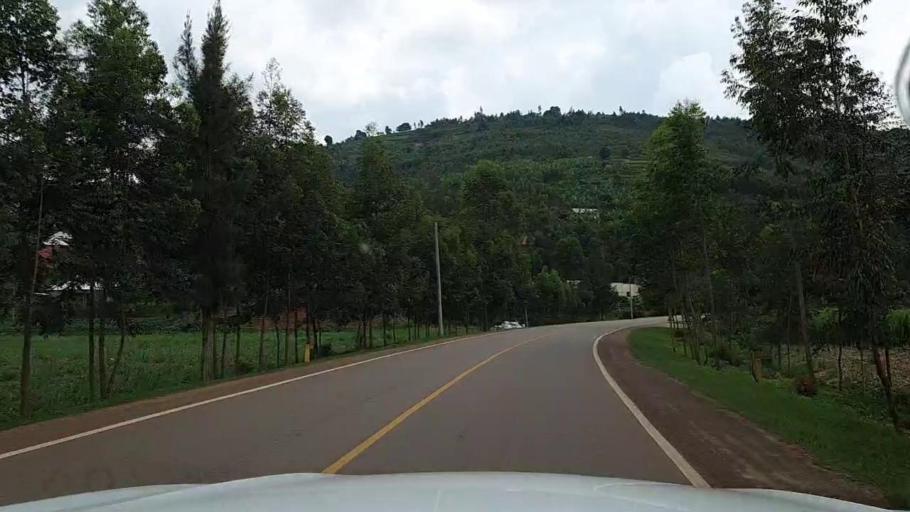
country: RW
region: Kigali
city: Kigali
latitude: -1.8121
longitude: 30.0976
